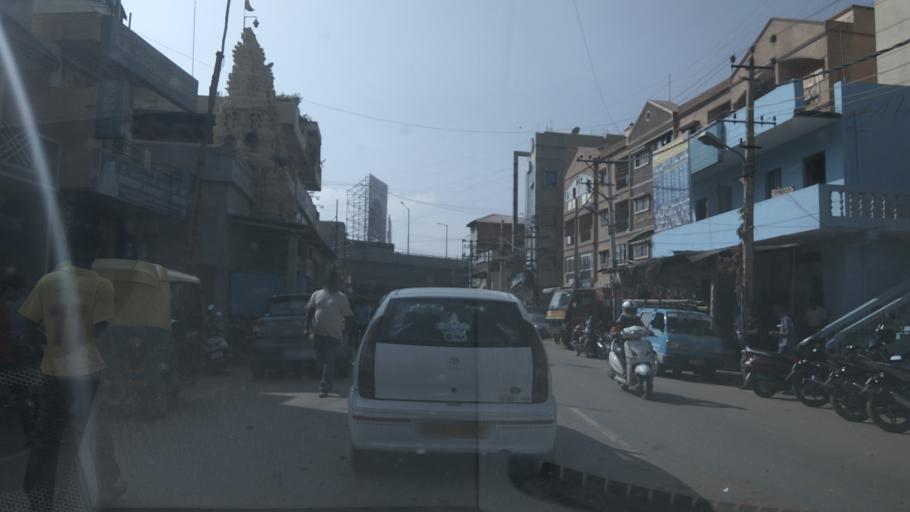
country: IN
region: Karnataka
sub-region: Bangalore Urban
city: Bangalore
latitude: 12.9268
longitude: 77.6764
